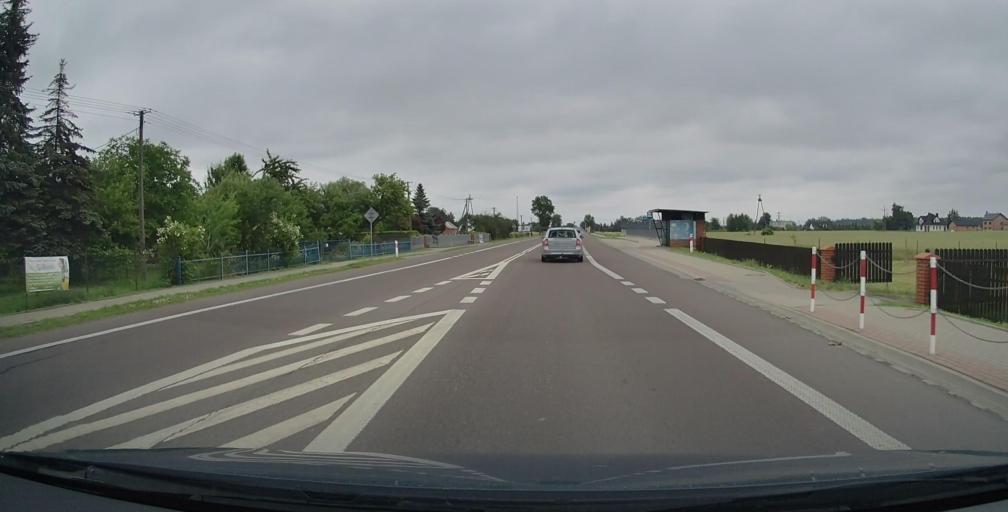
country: PL
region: Lublin Voivodeship
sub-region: Powiat bialski
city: Rzeczyca
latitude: 52.0325
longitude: 22.7027
